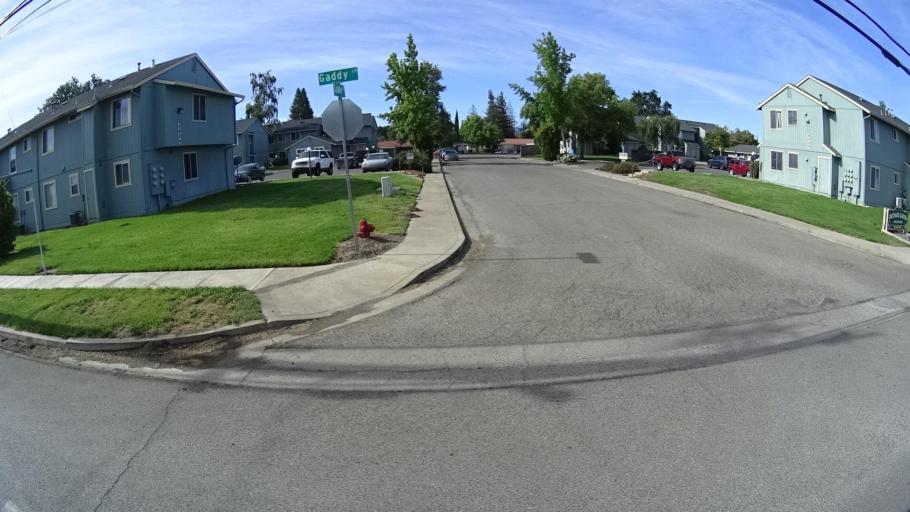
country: US
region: California
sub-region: Lake County
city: Kelseyville
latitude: 38.9820
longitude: -122.8333
